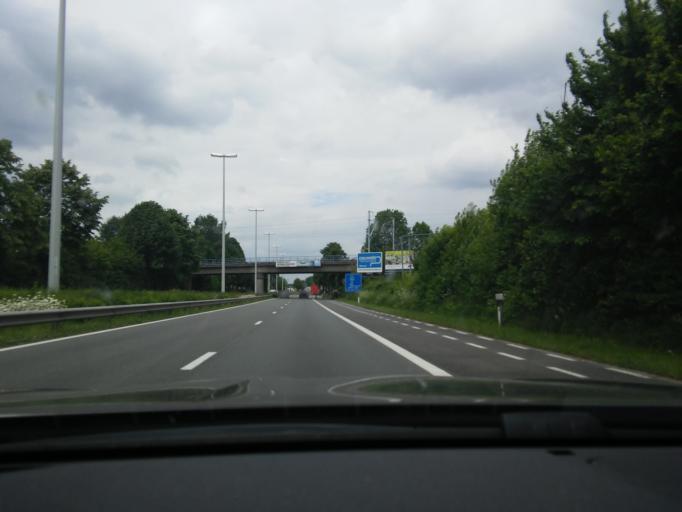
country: BE
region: Flanders
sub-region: Provincie Oost-Vlaanderen
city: Aalst
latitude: 50.9098
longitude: 4.0324
